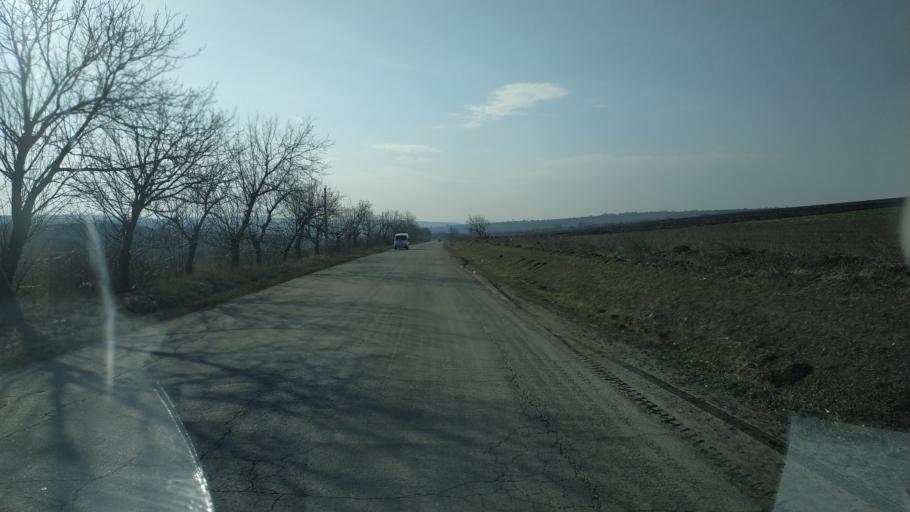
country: MD
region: Chisinau
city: Singera
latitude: 46.8489
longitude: 29.0237
